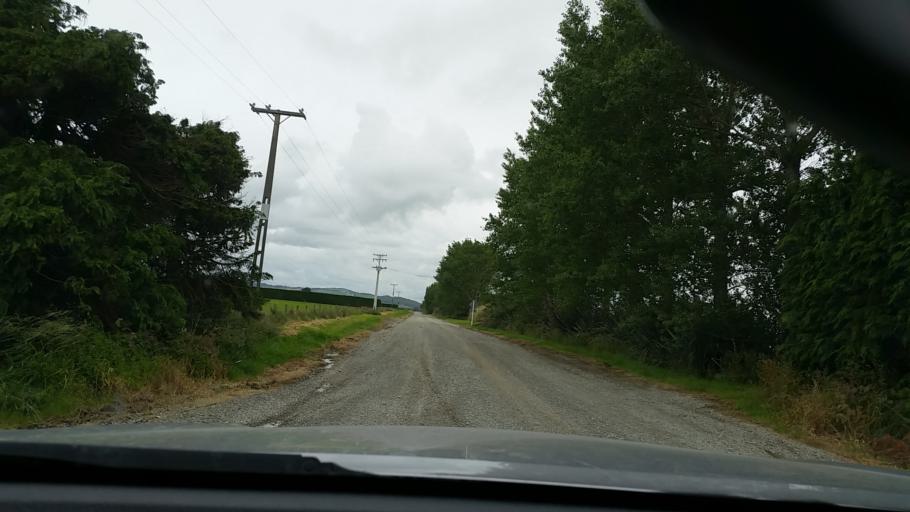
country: NZ
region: Southland
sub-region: Southland District
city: Winton
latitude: -46.2285
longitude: 168.3414
